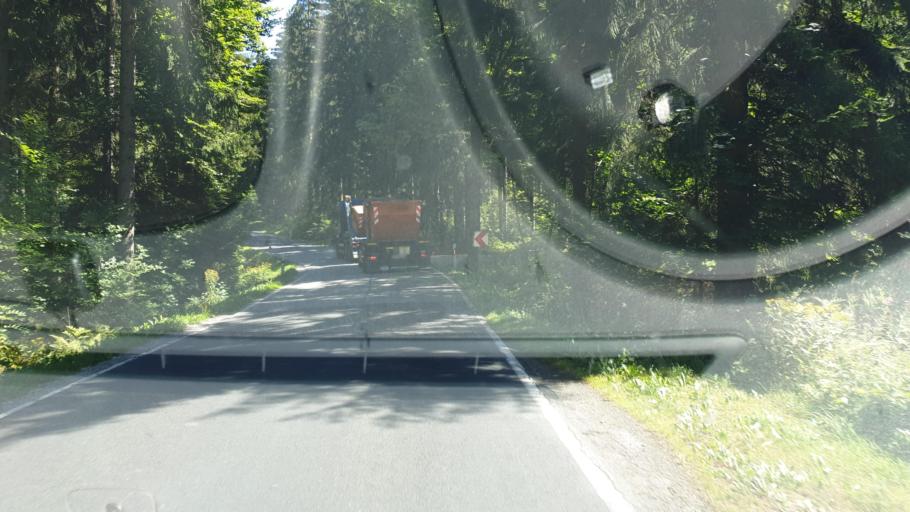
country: DE
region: Saxony
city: Sosa
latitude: 50.5055
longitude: 12.6799
